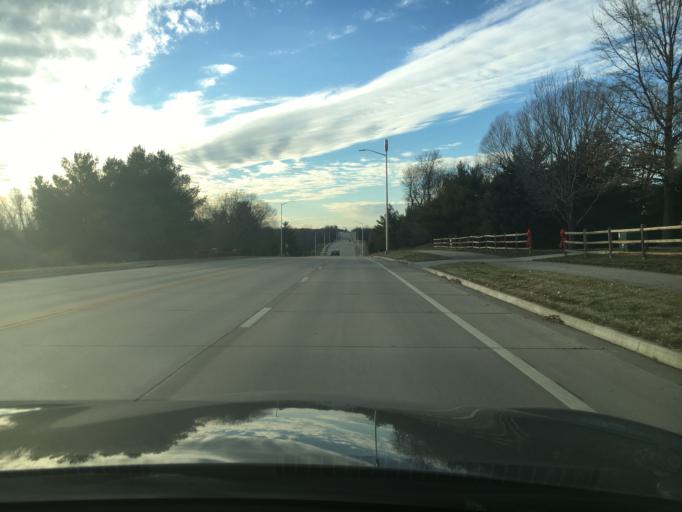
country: US
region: Kansas
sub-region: Johnson County
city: Leawood
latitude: 38.8693
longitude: -94.6342
